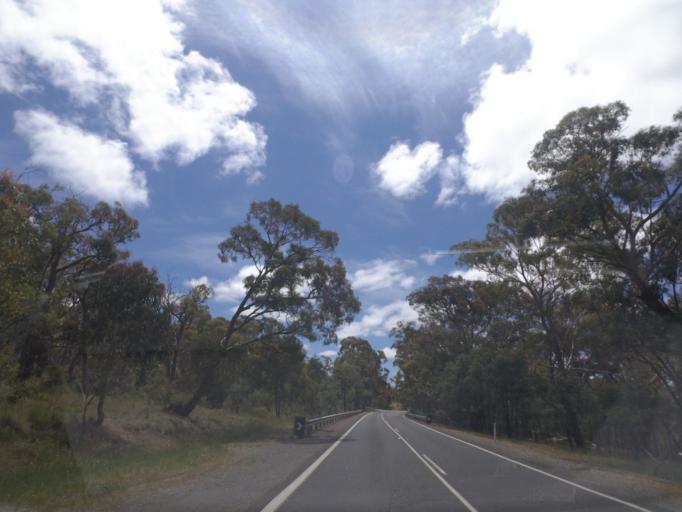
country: AU
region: Victoria
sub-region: Mount Alexander
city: Castlemaine
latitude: -37.3014
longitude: 144.1629
